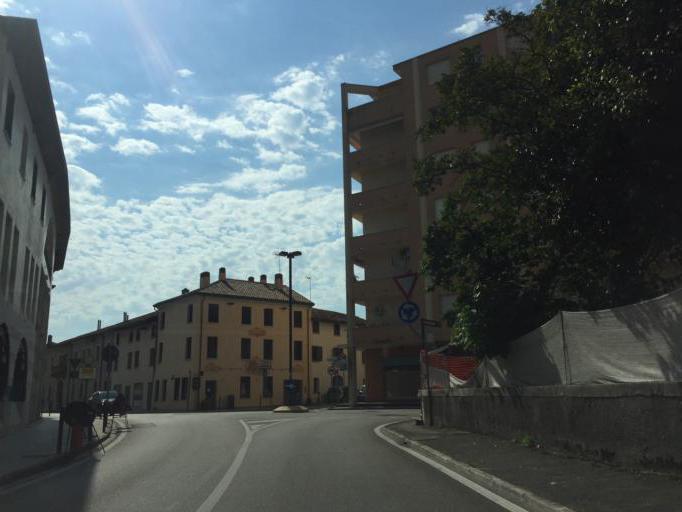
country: IT
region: Friuli Venezia Giulia
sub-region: Provincia di Pordenone
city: Sacile
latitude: 45.9542
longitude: 12.4963
